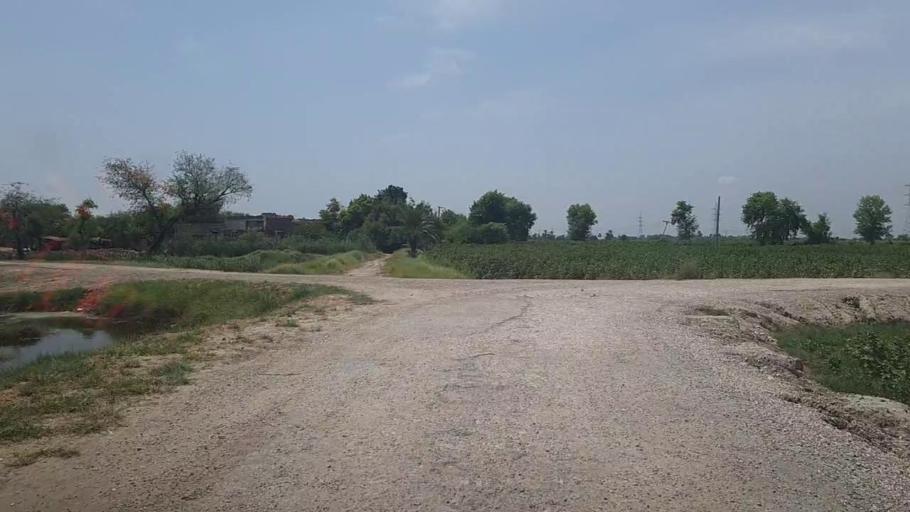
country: PK
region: Sindh
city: Ubauro
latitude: 28.1754
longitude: 69.7682
